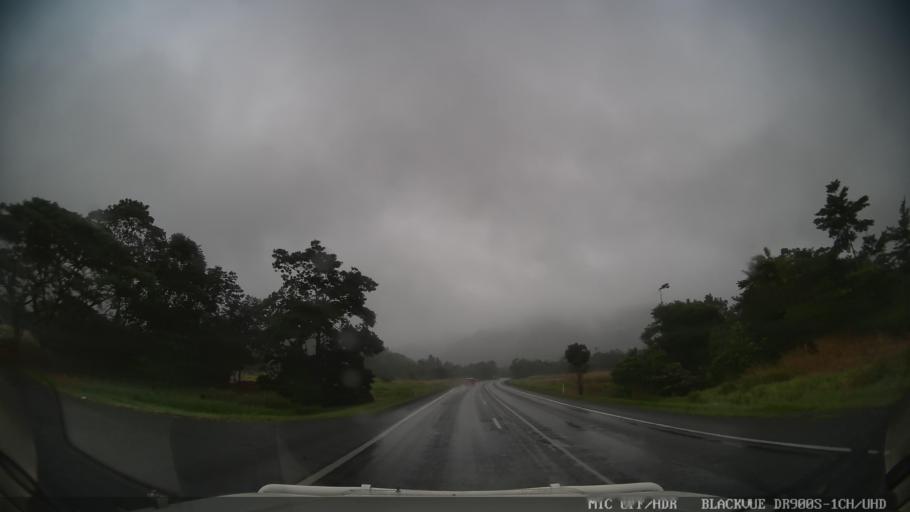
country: AU
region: Queensland
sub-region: Cassowary Coast
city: Innisfail
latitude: -17.8663
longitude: 145.9811
